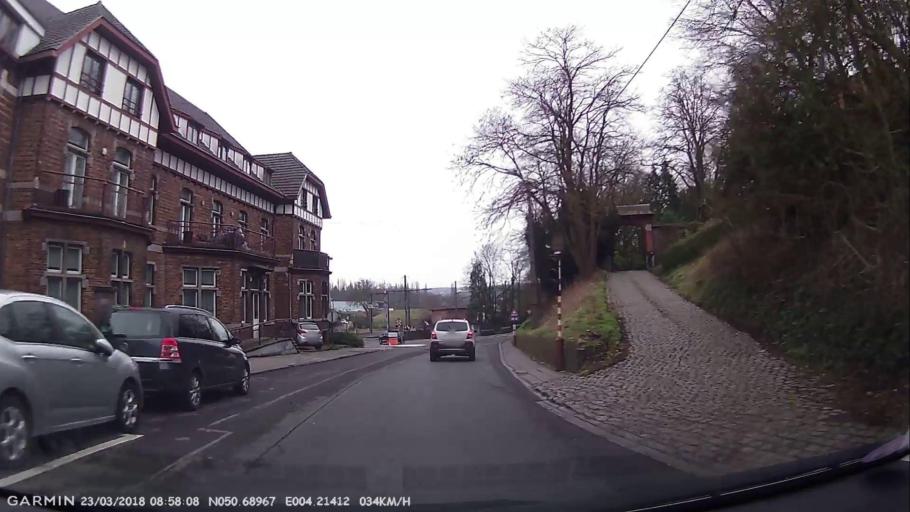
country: BE
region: Wallonia
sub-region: Province du Brabant Wallon
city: Tubize
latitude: 50.6896
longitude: 4.2142
